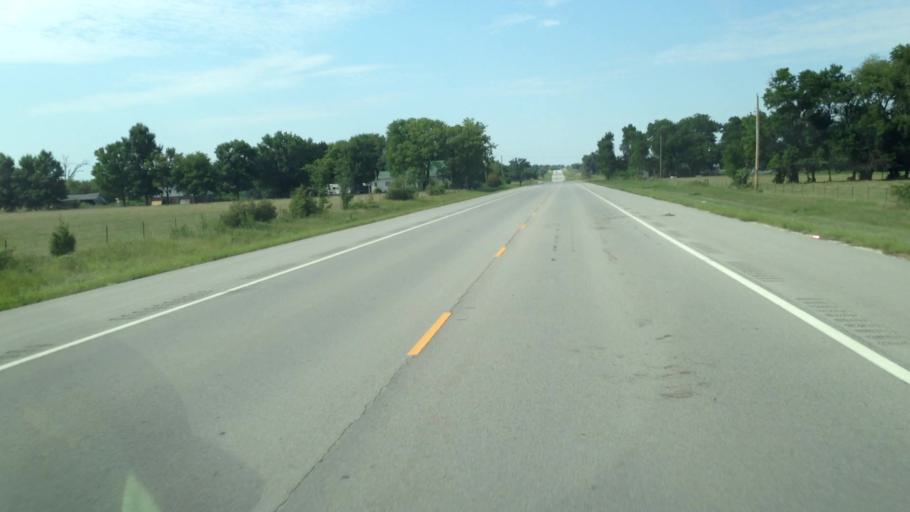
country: US
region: Kansas
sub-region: Labette County
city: Parsons
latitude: 37.2638
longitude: -95.2671
